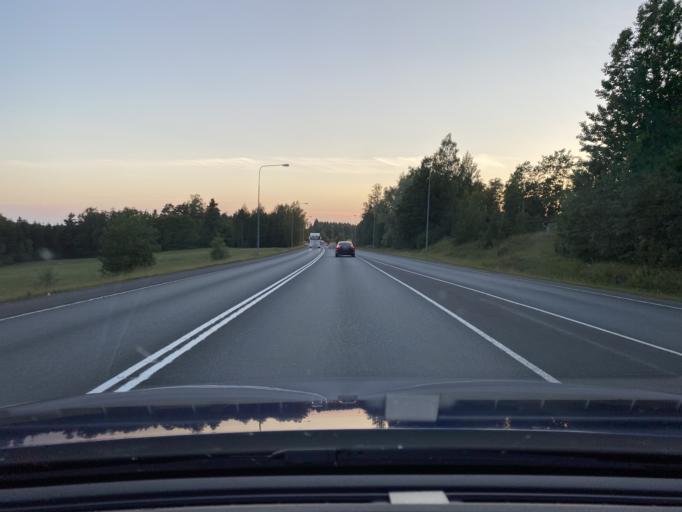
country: FI
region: Pirkanmaa
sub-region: Luoteis-Pirkanmaa
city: Ikaalinen
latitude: 61.7554
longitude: 23.0570
